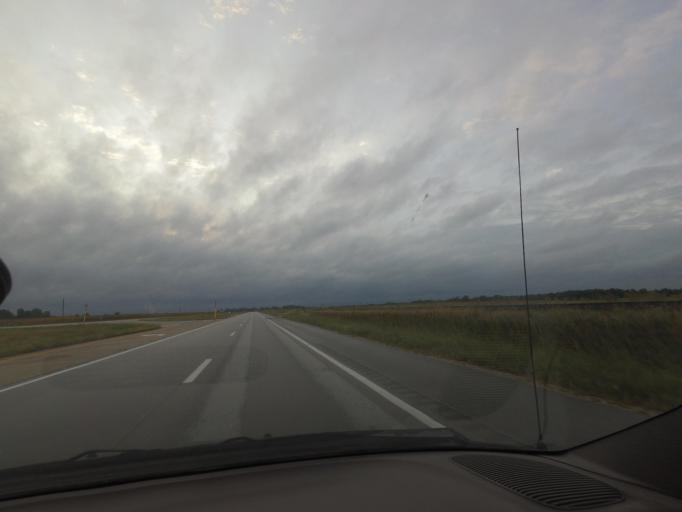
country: US
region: Missouri
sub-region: Shelby County
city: Shelbina
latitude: 39.6772
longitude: -91.9699
